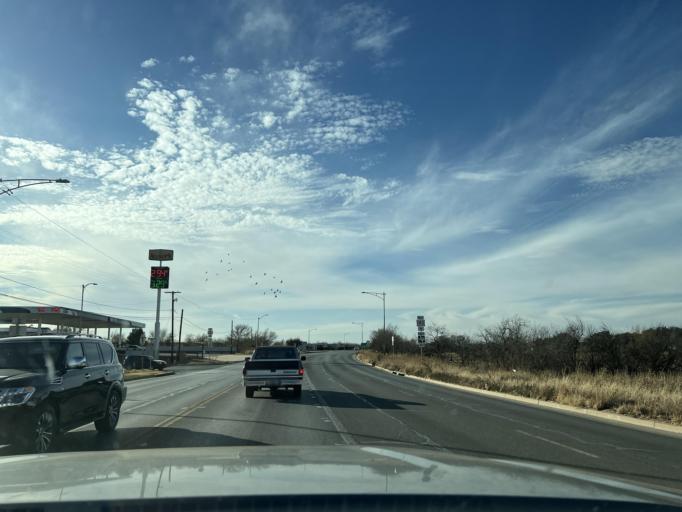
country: US
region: Texas
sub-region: Scurry County
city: Snyder
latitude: 32.7173
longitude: -100.9316
